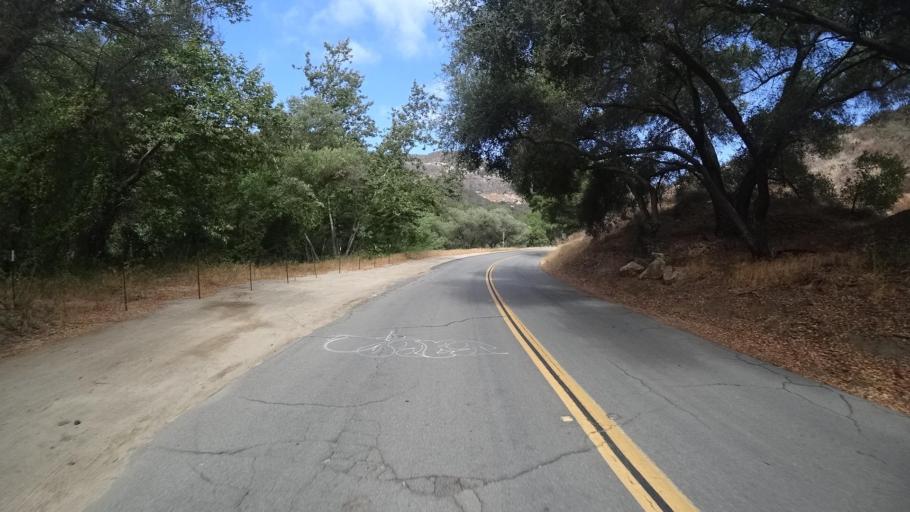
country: US
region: California
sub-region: San Diego County
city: Fallbrook
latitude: 33.4152
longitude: -117.2460
